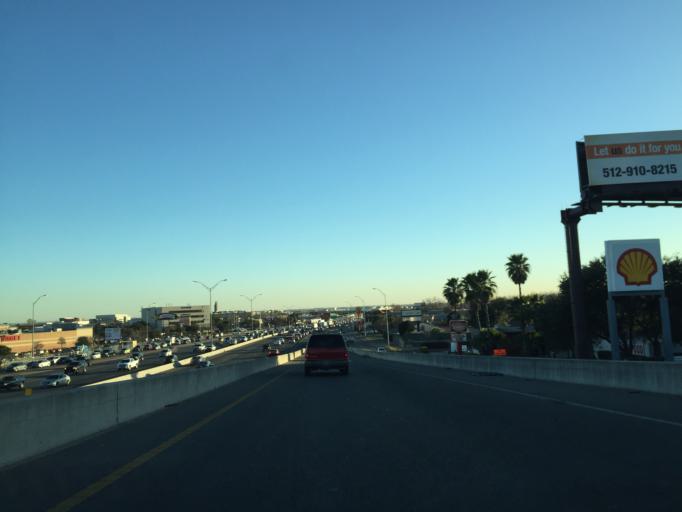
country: US
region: Texas
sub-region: Travis County
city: Austin
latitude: 30.3187
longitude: -97.7075
